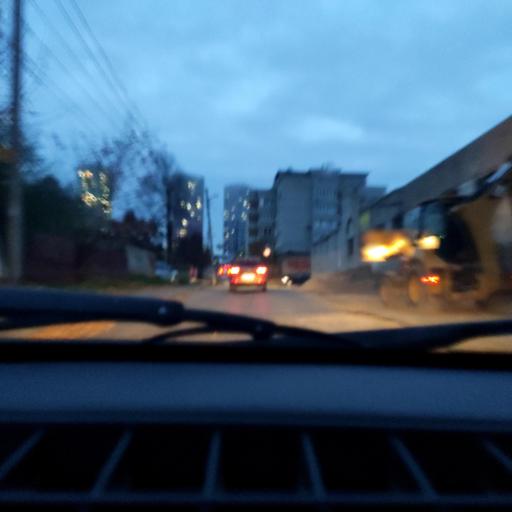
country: RU
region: Bashkortostan
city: Ufa
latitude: 54.7729
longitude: 56.0462
